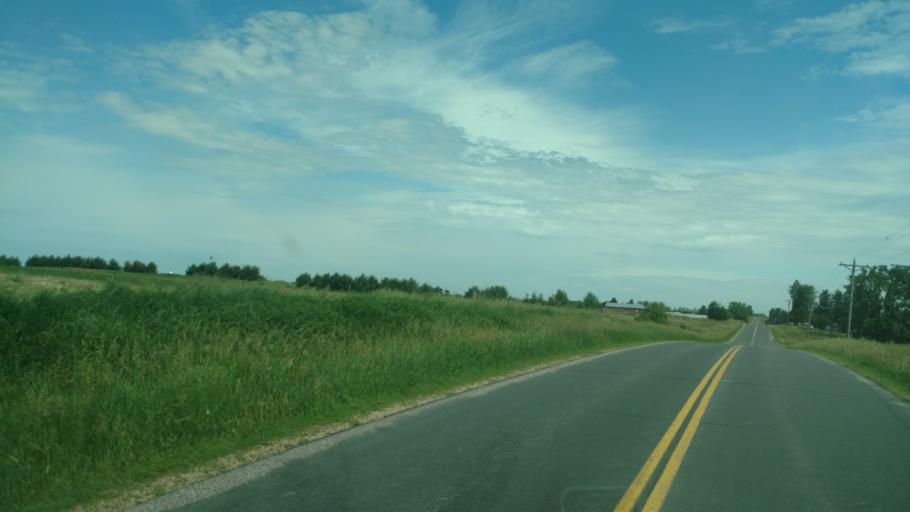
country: US
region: Wisconsin
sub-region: Vernon County
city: Hillsboro
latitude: 43.7500
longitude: -90.4329
